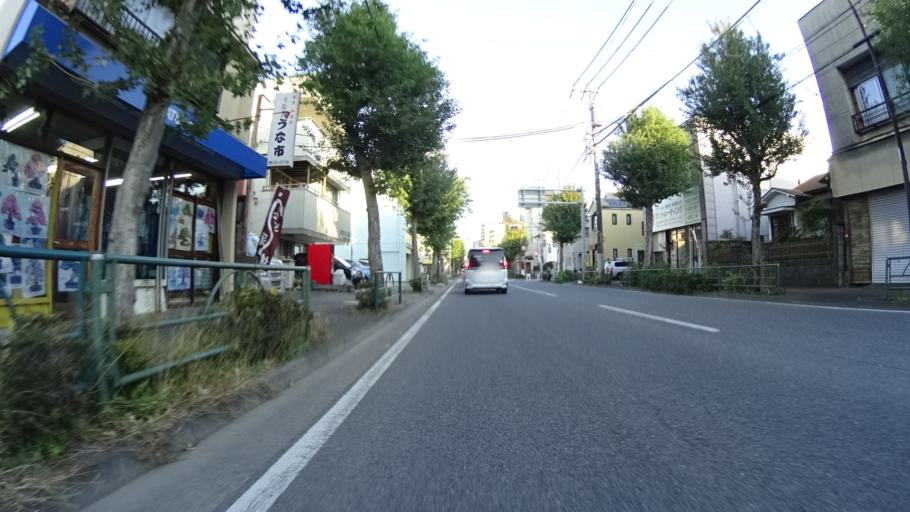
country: JP
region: Tokyo
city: Hachioji
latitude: 35.6615
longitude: 139.3149
